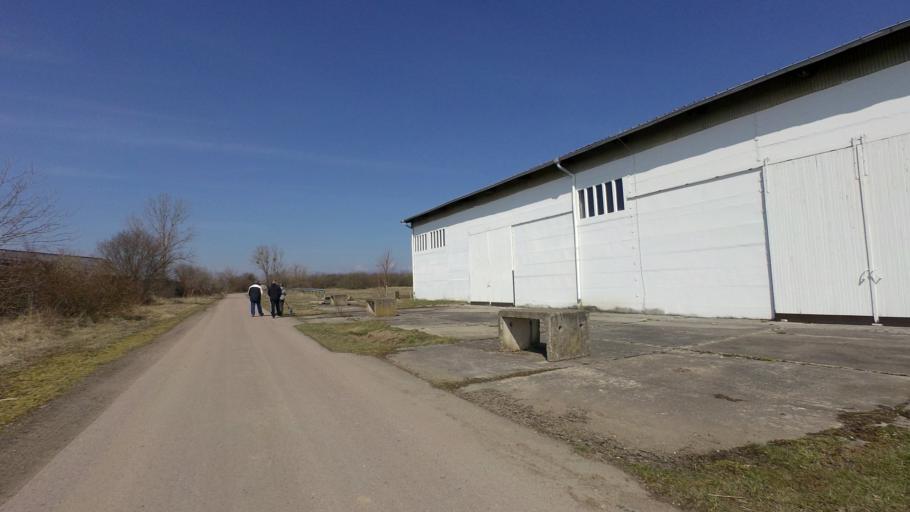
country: DE
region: Saxony-Anhalt
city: Vockerode
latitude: 51.8529
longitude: 12.3434
